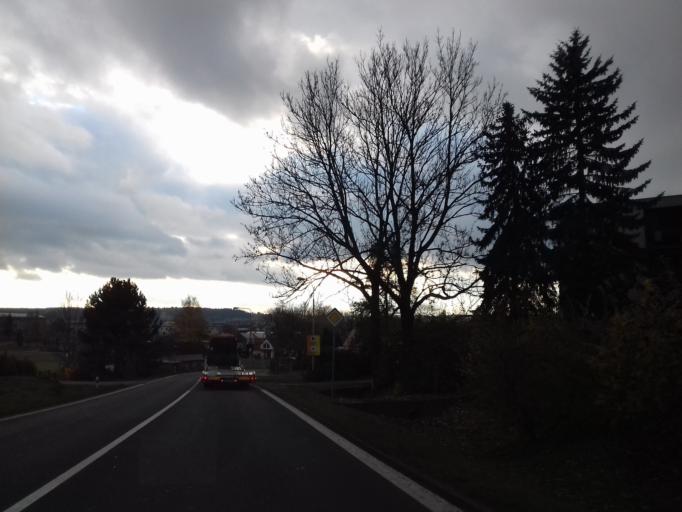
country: CZ
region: Pardubicky
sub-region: Okres Svitavy
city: Policka
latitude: 49.7194
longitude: 16.2858
